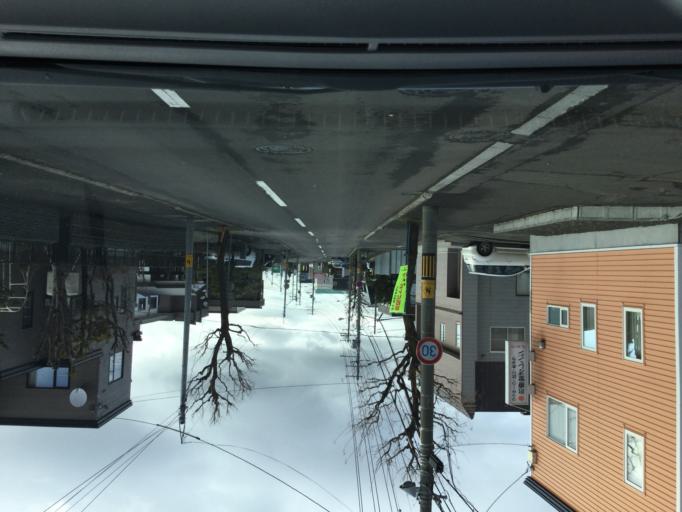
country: JP
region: Hokkaido
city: Sapporo
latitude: 43.0232
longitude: 141.4288
